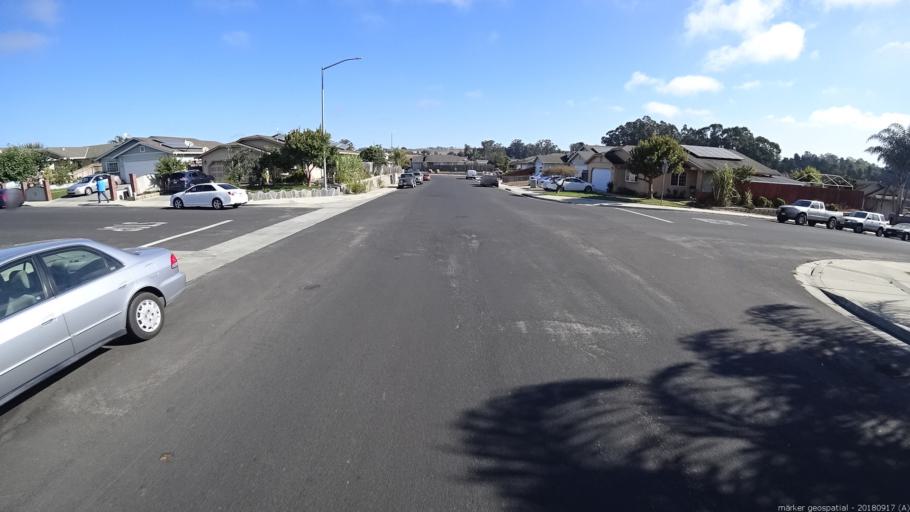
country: US
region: California
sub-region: Monterey County
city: Castroville
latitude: 36.7862
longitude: -121.7268
